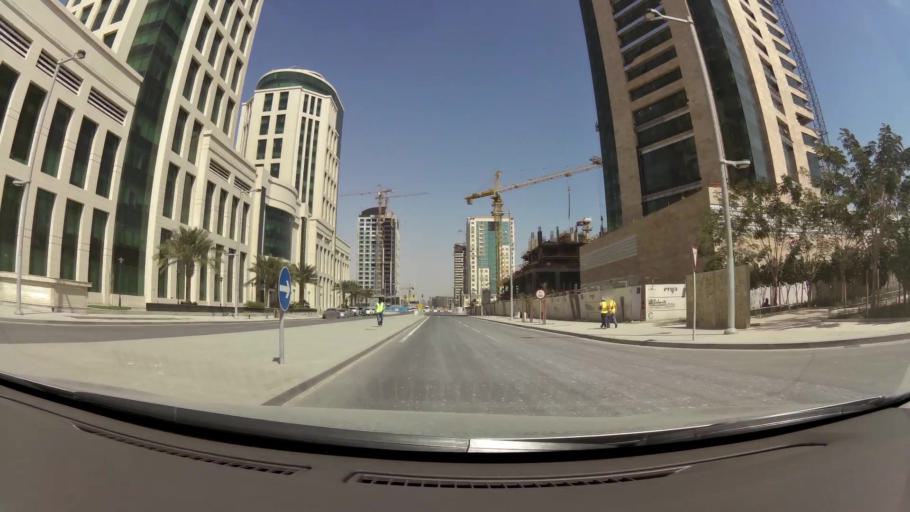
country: QA
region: Baladiyat ad Dawhah
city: Doha
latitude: 25.3928
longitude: 51.5224
